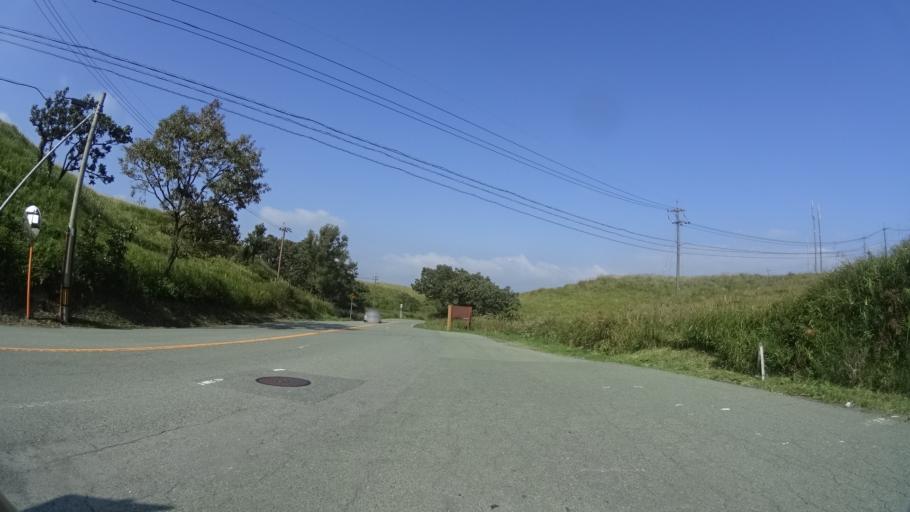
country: JP
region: Kumamoto
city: Aso
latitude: 33.0095
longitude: 131.0666
